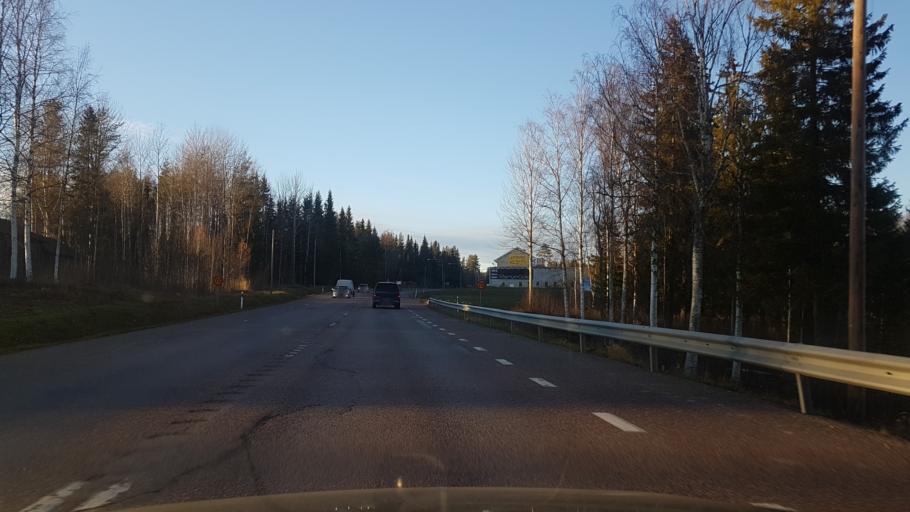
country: SE
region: Dalarna
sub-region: Faluns Kommun
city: Bjursas
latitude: 60.7204
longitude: 15.4541
